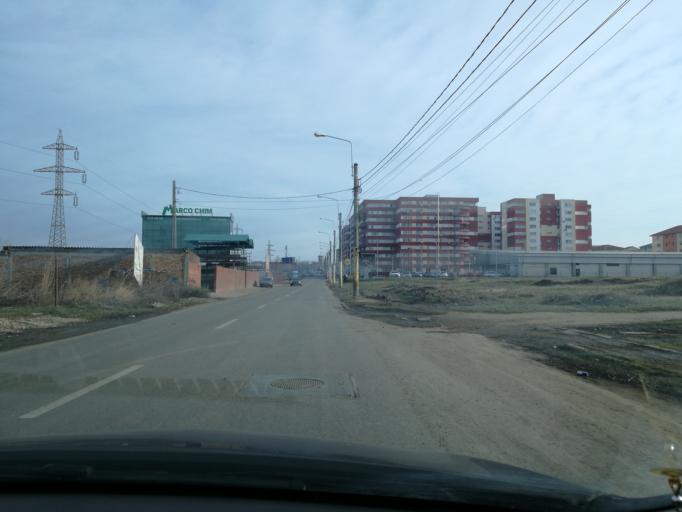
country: RO
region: Constanta
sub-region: Municipiul Constanta
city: Constanta
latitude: 44.1899
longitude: 28.6089
